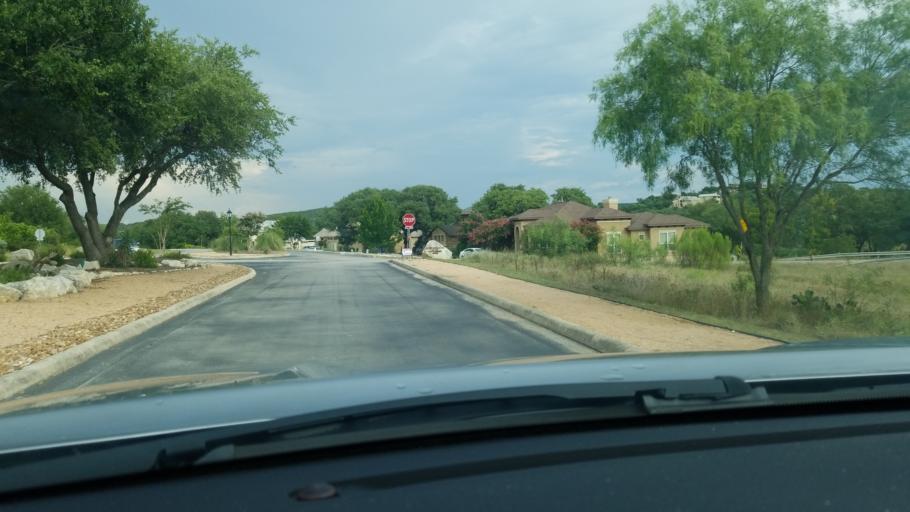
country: US
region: Texas
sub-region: Comal County
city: Bulverde
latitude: 29.8477
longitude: -98.4033
